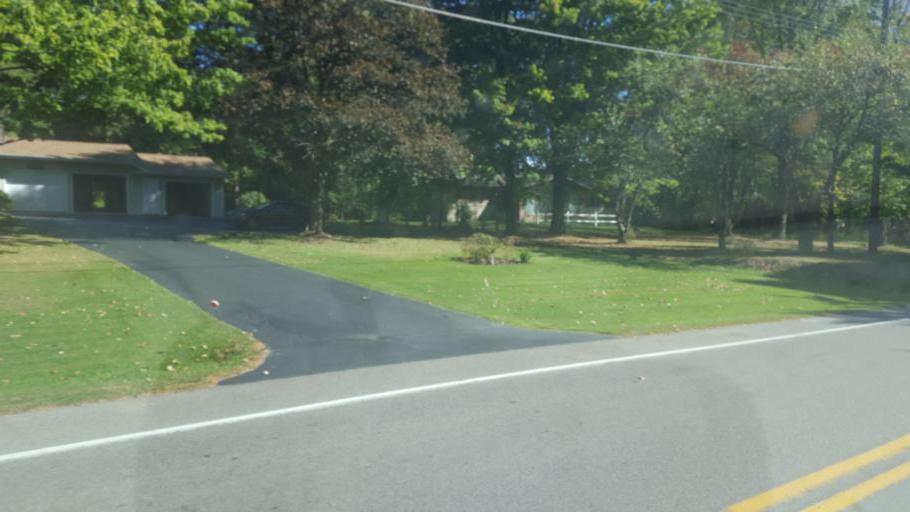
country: US
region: Pennsylvania
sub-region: Mercer County
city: Reynolds Heights
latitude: 41.3655
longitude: -80.3560
